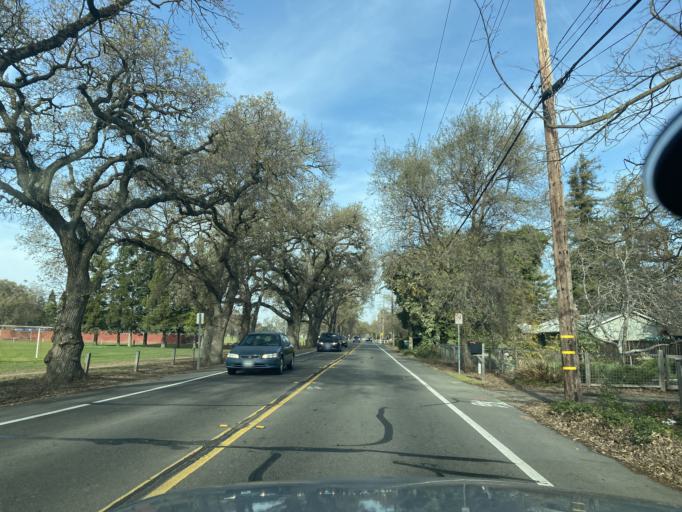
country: US
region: California
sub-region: Sacramento County
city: Elk Grove
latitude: 38.3909
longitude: -121.3714
